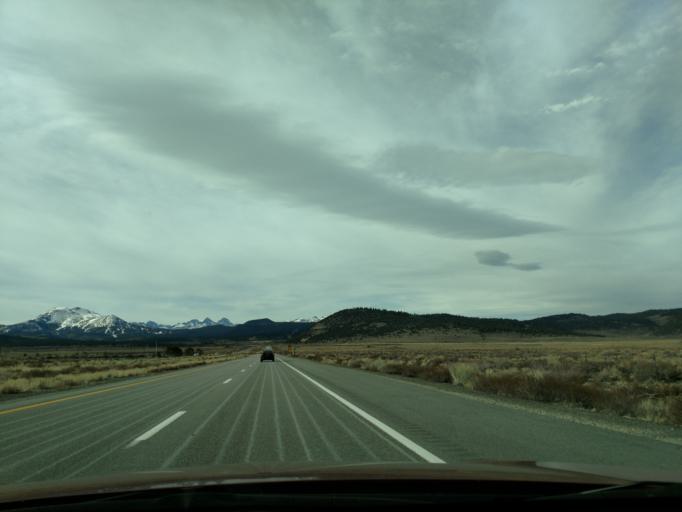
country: US
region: California
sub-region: Mono County
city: Mammoth Lakes
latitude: 37.6279
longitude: -118.8606
